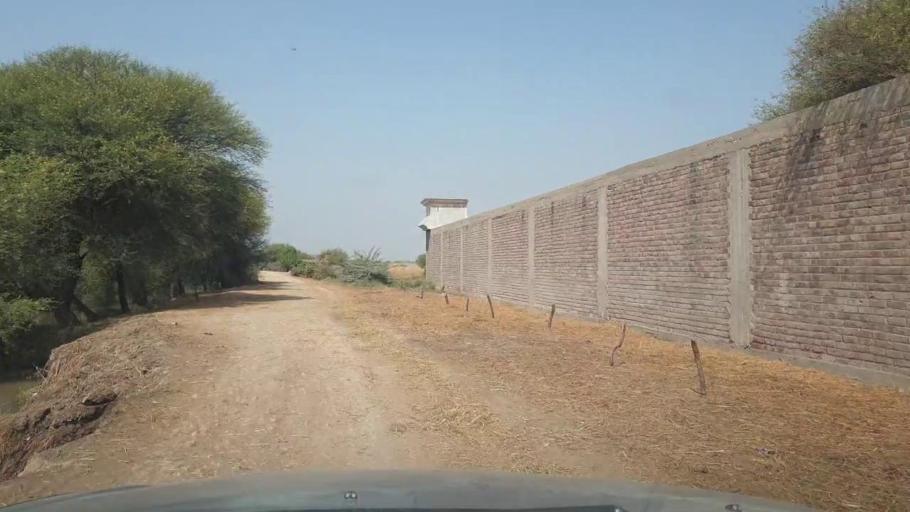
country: PK
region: Sindh
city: Bulri
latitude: 24.8849
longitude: 68.3957
